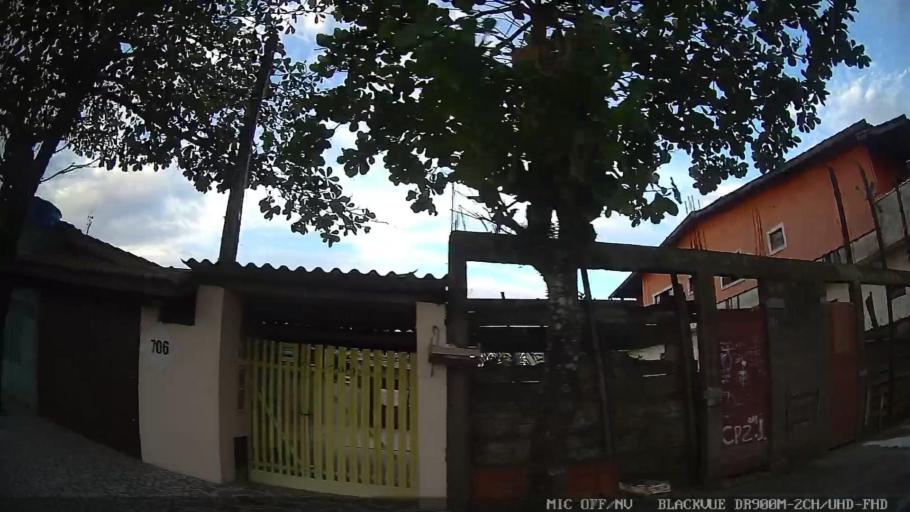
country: BR
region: Sao Paulo
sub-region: Itanhaem
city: Itanhaem
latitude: -24.1626
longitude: -46.7809
